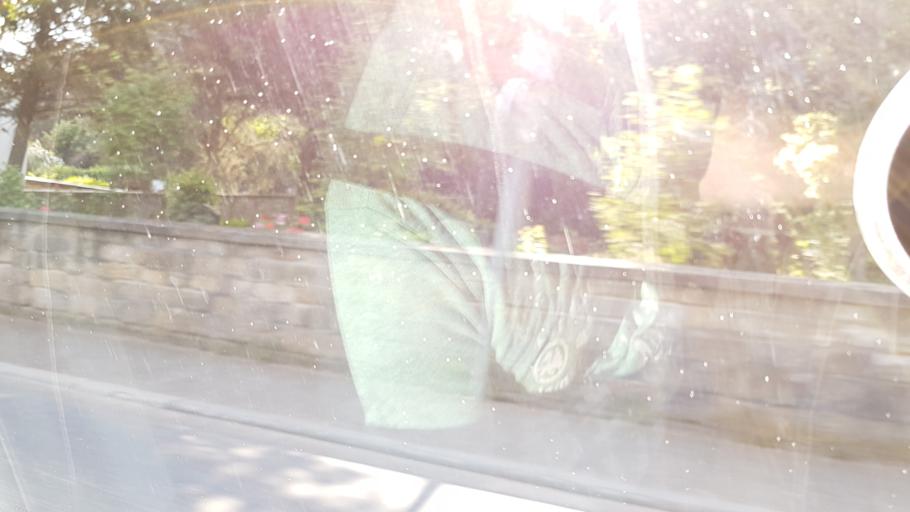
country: DE
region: Rheinland-Pfalz
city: Odenbach
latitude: 49.6852
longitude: 7.6486
